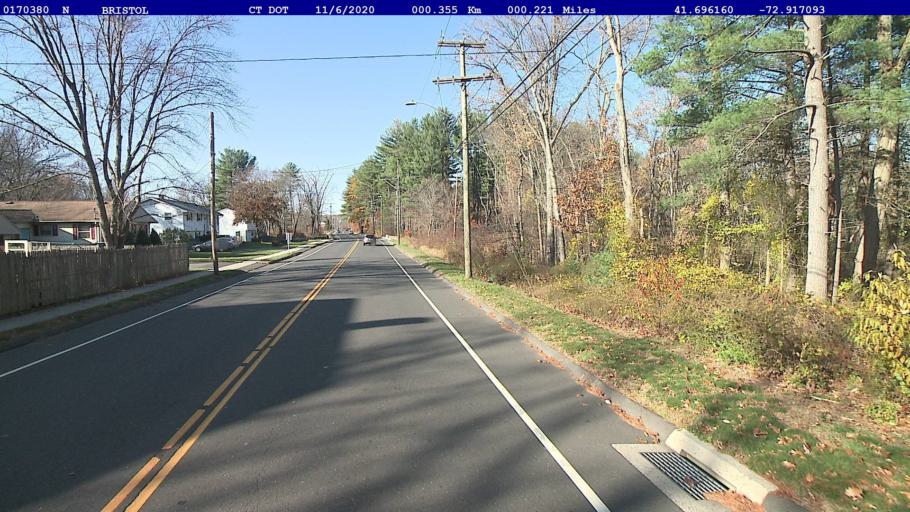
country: US
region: Connecticut
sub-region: Hartford County
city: Bristol
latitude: 41.6962
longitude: -72.9171
